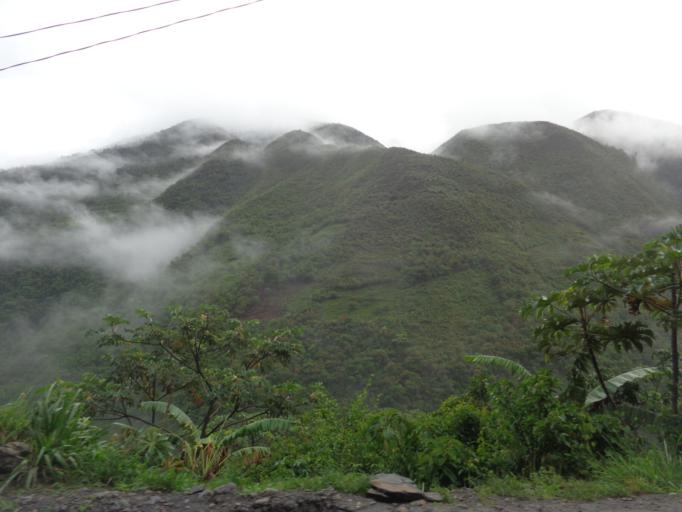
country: BO
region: La Paz
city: Coripata
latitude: -16.3999
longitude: -67.7188
